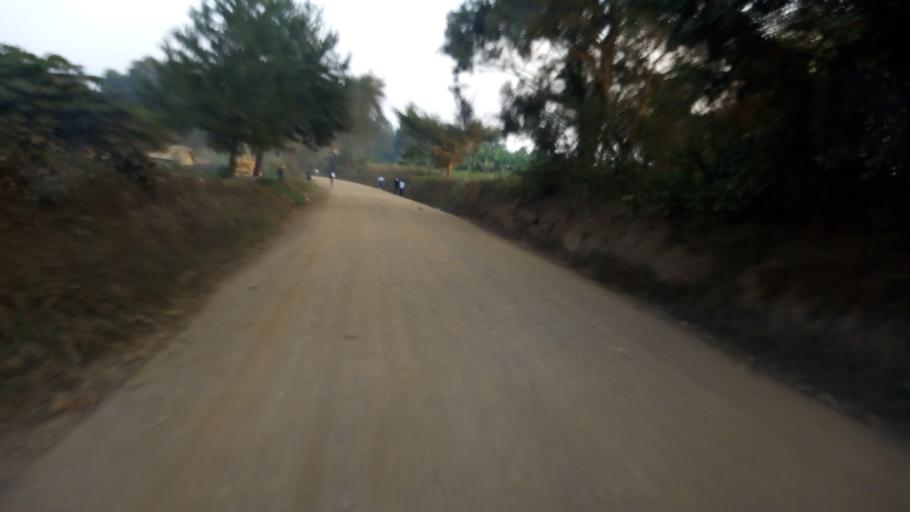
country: UG
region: Western Region
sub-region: Rukungiri District
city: Rukungiri
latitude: -0.7702
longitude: 29.9264
